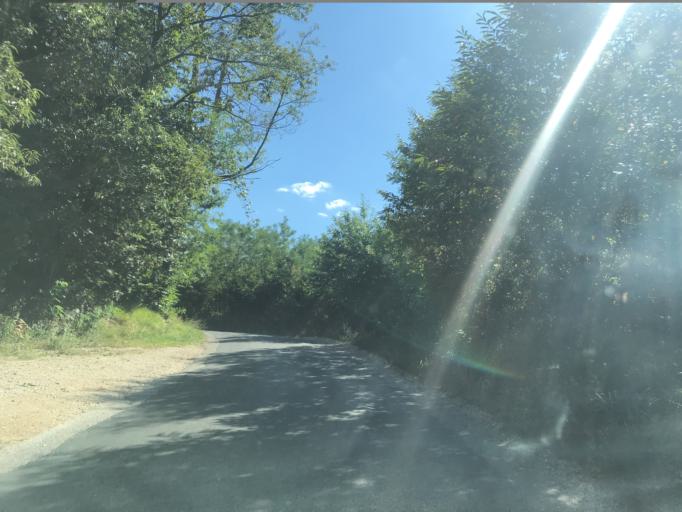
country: FR
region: Aquitaine
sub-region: Departement de la Dordogne
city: Sarlat-la-Caneda
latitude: 44.9269
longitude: 1.2024
